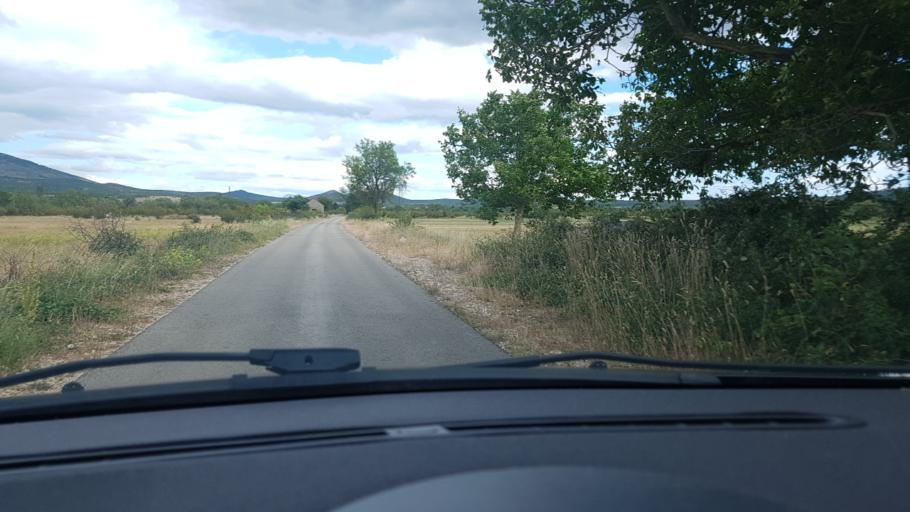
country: HR
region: Sibensko-Kniniska
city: Kistanje
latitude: 44.1091
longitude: 15.9285
